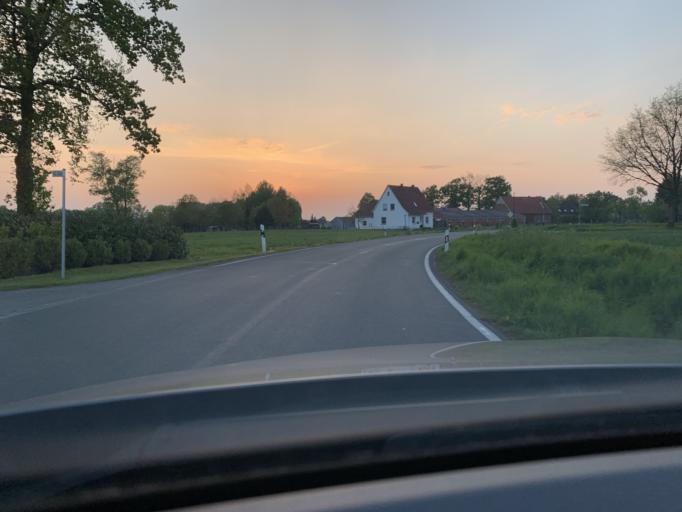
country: DE
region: North Rhine-Westphalia
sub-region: Regierungsbezirk Detmold
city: Langenberg
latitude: 51.7876
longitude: 8.3731
